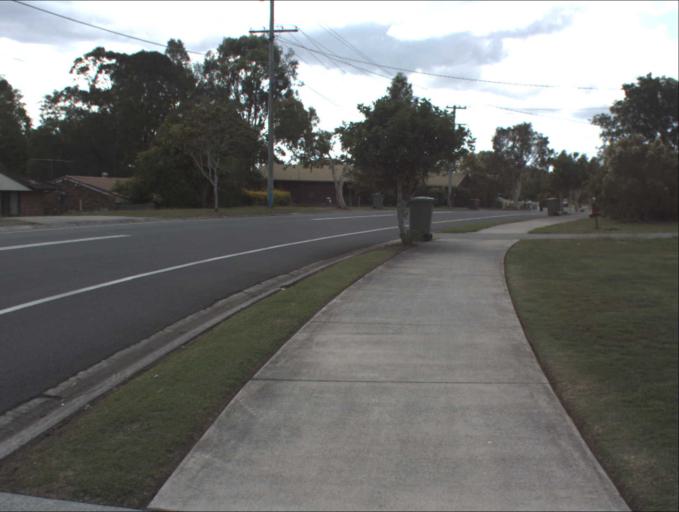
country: AU
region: Queensland
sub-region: Logan
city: Waterford West
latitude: -27.6891
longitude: 153.1507
